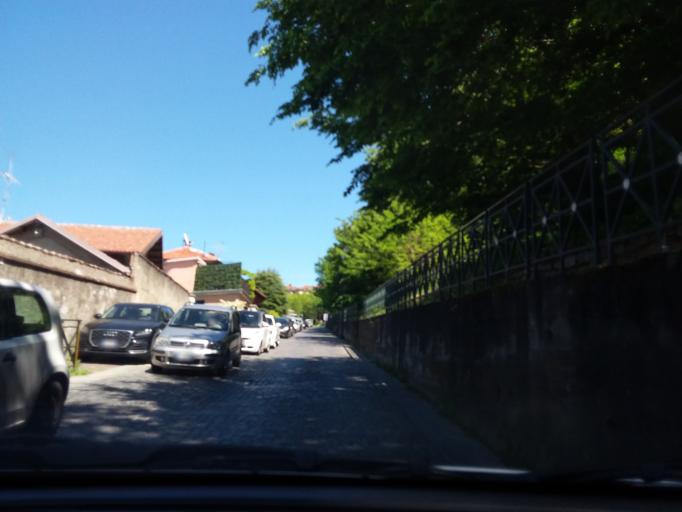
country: IT
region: Piedmont
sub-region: Provincia di Torino
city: Rivoli
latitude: 45.0696
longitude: 7.5062
